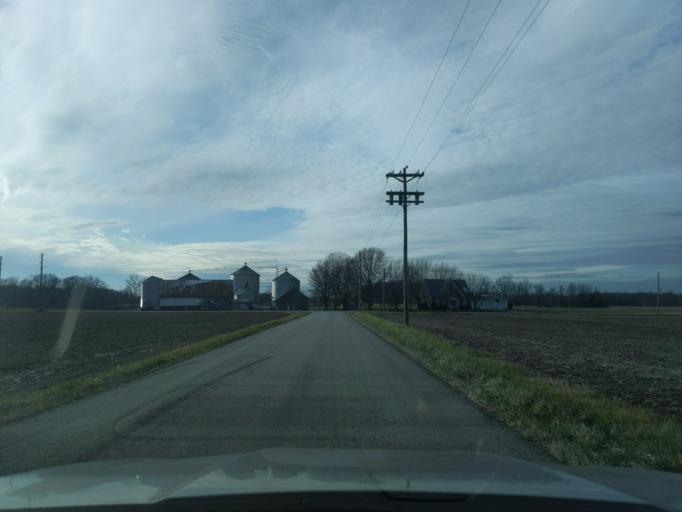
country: US
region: Indiana
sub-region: Decatur County
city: Westport
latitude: 39.2175
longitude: -85.4637
